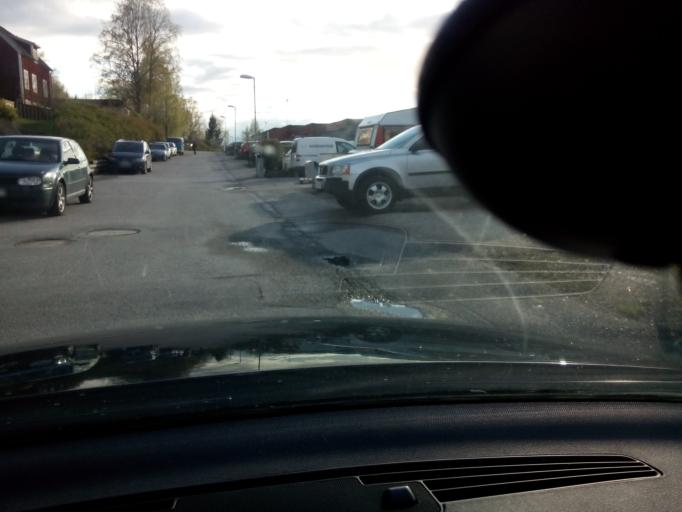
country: SE
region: Soedermanland
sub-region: Nykopings Kommun
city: Nykoping
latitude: 58.7801
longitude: 17.0966
